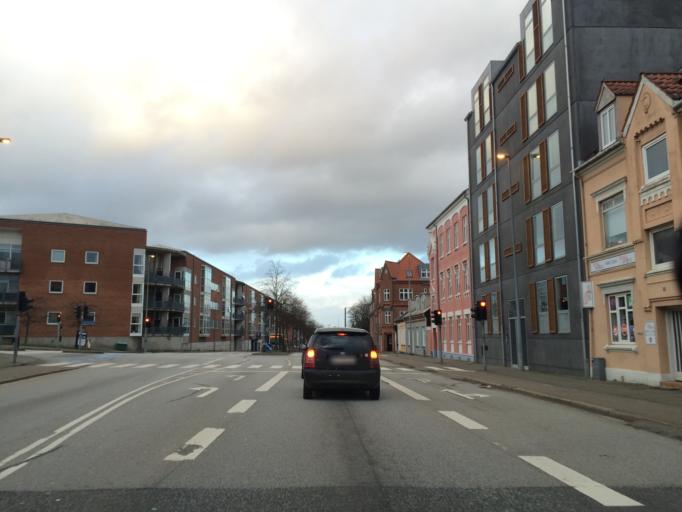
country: DK
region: Central Jutland
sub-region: Silkeborg Kommune
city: Silkeborg
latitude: 56.1674
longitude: 9.5519
